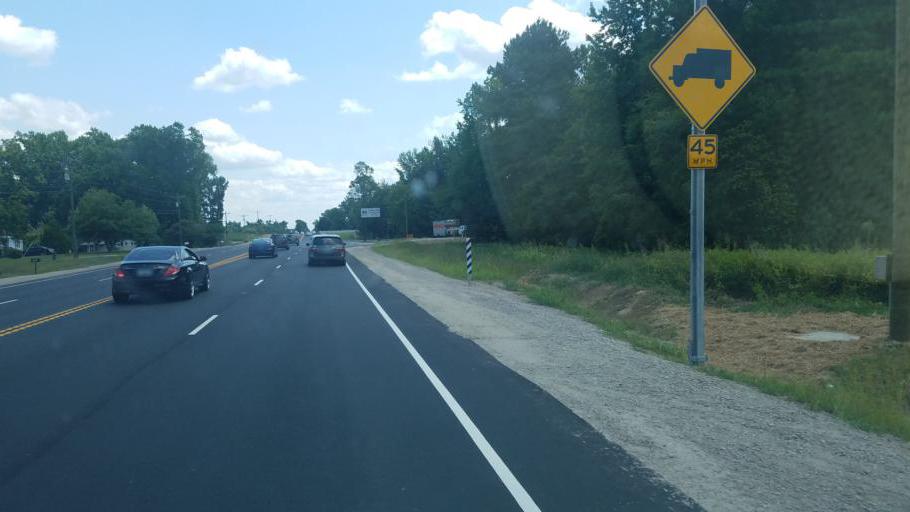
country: US
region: Virginia
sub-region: Prince George County
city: Prince George
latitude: 37.1646
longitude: -77.2888
